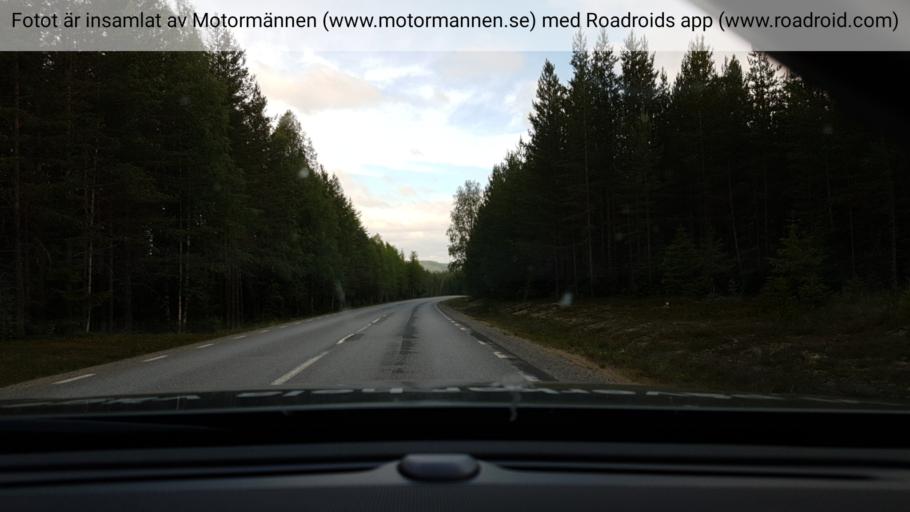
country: SE
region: Vaesterbotten
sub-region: Vindelns Kommun
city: Vindeln
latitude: 64.2541
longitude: 19.6350
